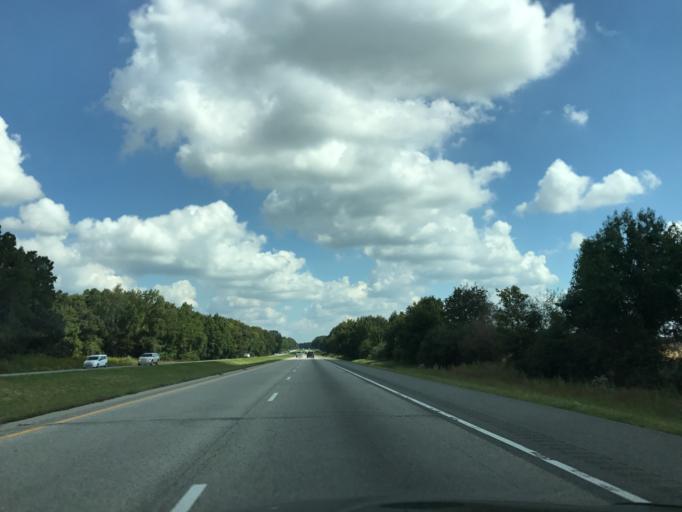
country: US
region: Maryland
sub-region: Queen Anne's County
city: Centreville
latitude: 38.9994
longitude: -76.1242
